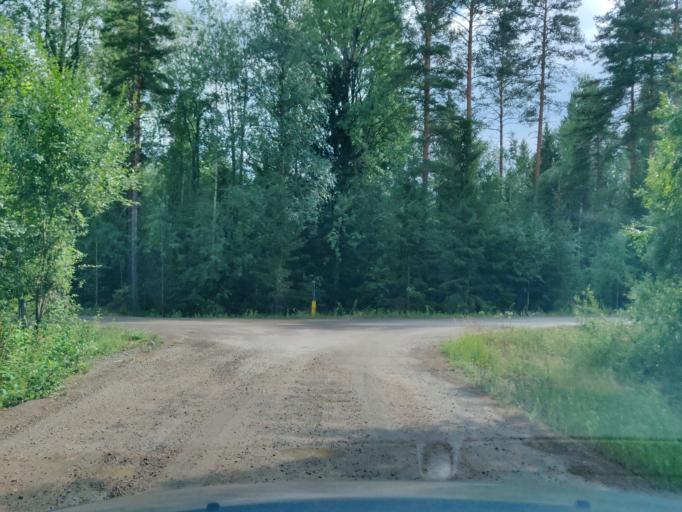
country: SE
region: Vaermland
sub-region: Hagfors Kommun
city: Hagfors
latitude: 59.9734
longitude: 13.5485
